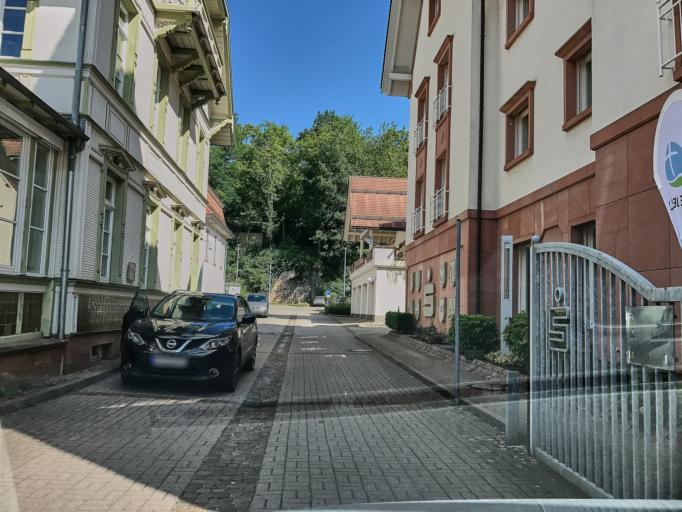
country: DE
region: Baden-Wuerttemberg
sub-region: Freiburg Region
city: Biberach
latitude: 48.3475
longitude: 8.0655
